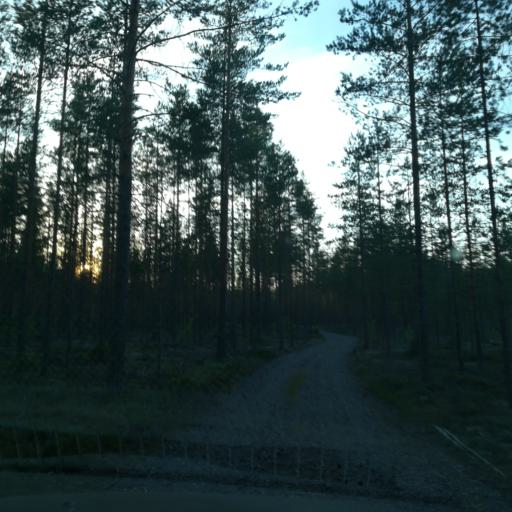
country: FI
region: Southern Savonia
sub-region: Mikkeli
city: Puumala
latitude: 61.4347
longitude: 28.4616
